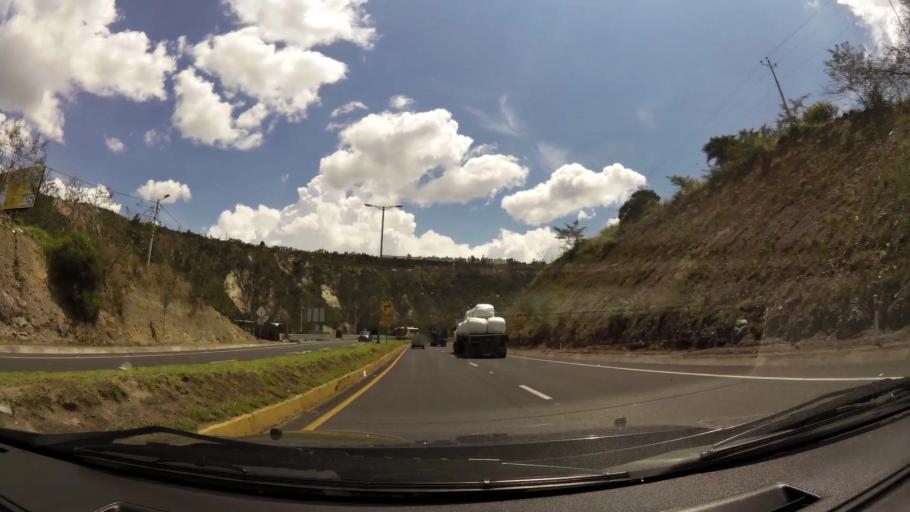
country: EC
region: Pichincha
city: Quito
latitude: -0.1005
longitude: -78.4129
